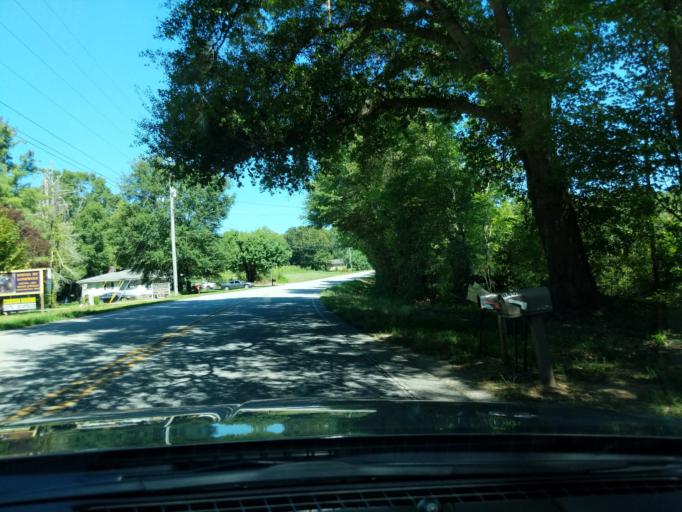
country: US
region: Georgia
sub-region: Habersham County
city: Demorest
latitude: 34.5857
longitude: -83.6173
